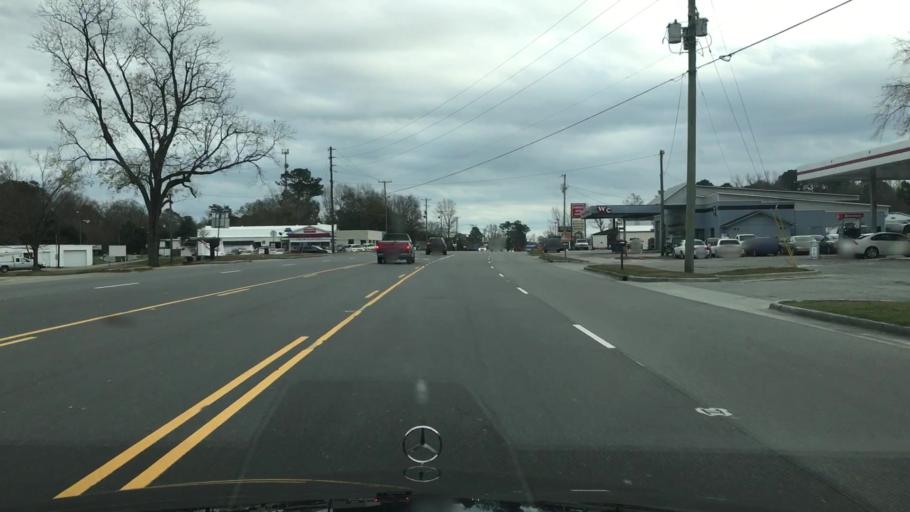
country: US
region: North Carolina
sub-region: Onslow County
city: Richlands
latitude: 34.9028
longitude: -77.5543
